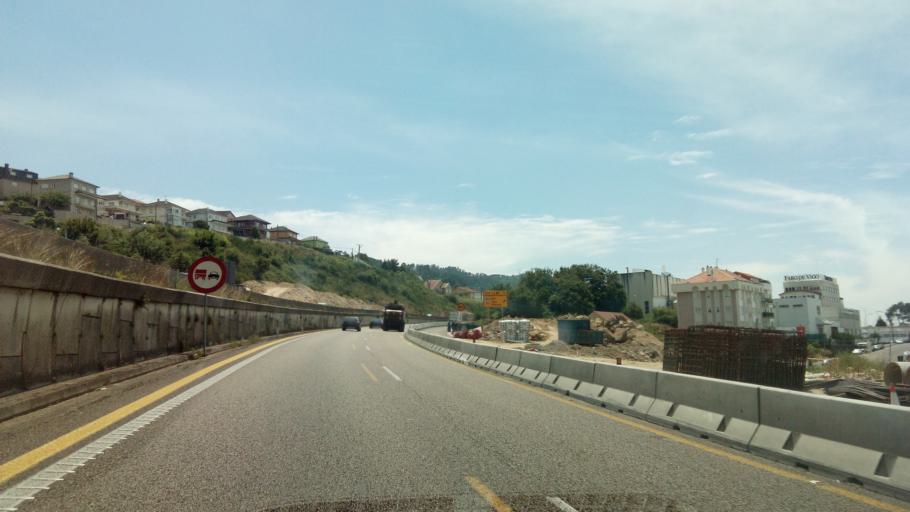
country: ES
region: Galicia
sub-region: Provincia de Pontevedra
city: Redondela
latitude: 42.2696
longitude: -8.6637
